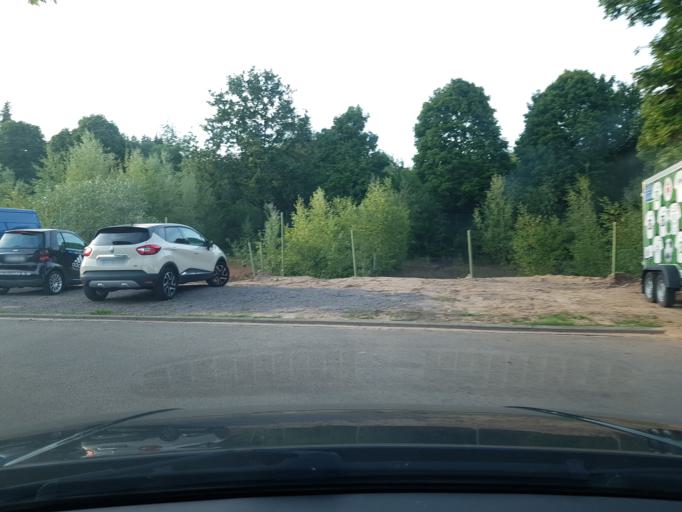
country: DE
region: Saarland
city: Saarbrucken
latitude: 49.2196
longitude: 6.9804
